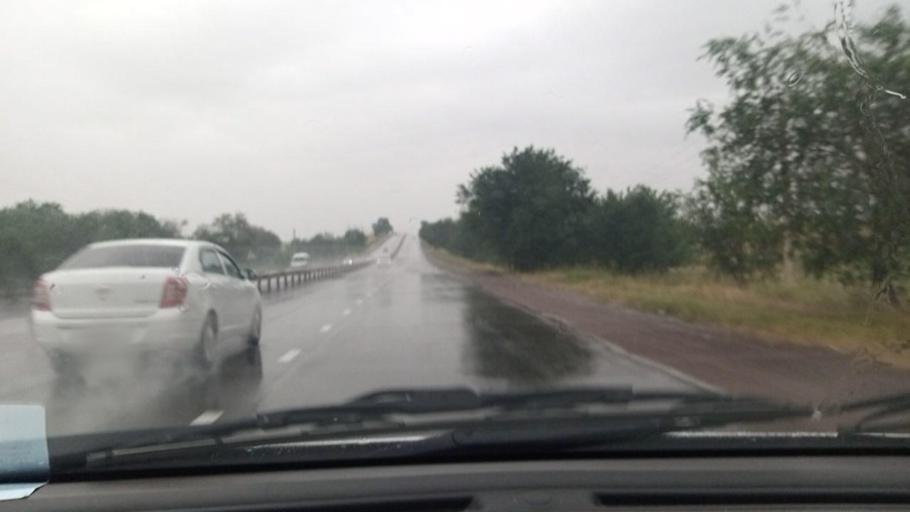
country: UZ
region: Toshkent
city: Ohangaron
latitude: 40.9535
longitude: 69.5668
